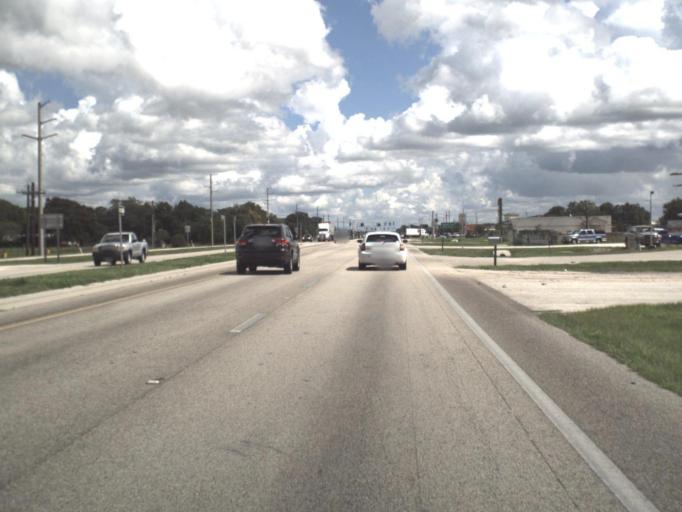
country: US
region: Florida
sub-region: DeSoto County
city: Arcadia
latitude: 27.2089
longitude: -81.8375
